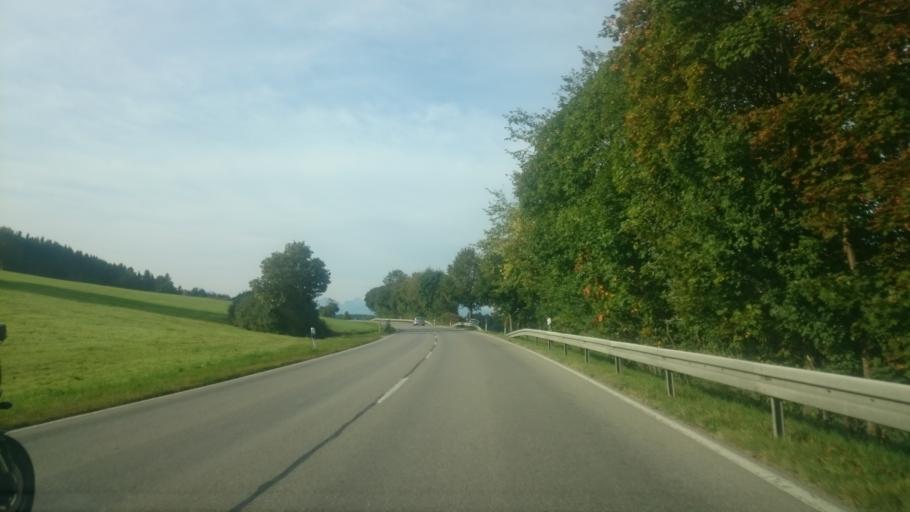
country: DE
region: Bavaria
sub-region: Upper Bavaria
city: Peiting
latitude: 47.7520
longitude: 10.8953
